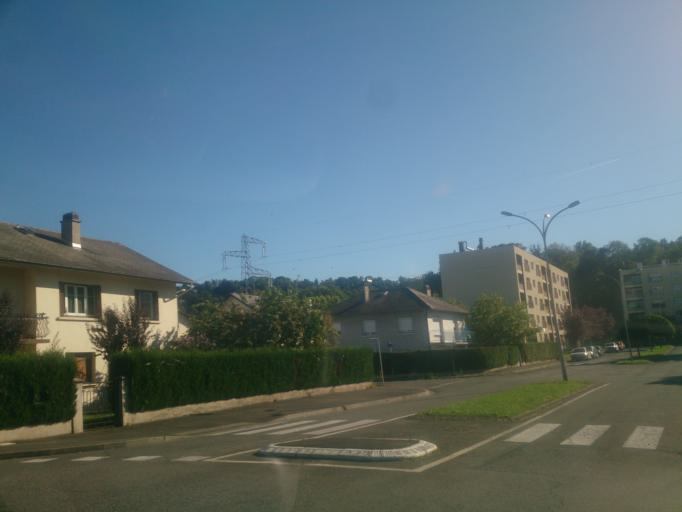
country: FR
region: Midi-Pyrenees
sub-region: Departement des Hautes-Pyrenees
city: Bagneres-de-Bigorre
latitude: 43.0755
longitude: 0.1546
